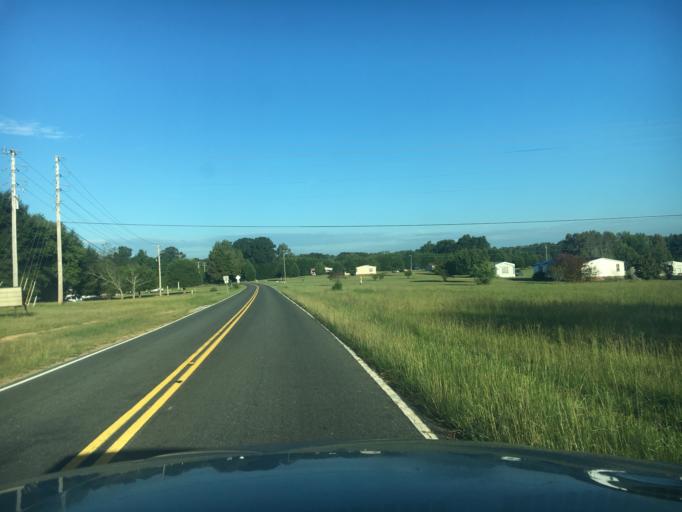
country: US
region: South Carolina
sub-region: Spartanburg County
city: Woodruff
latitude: 34.6299
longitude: -82.0310
